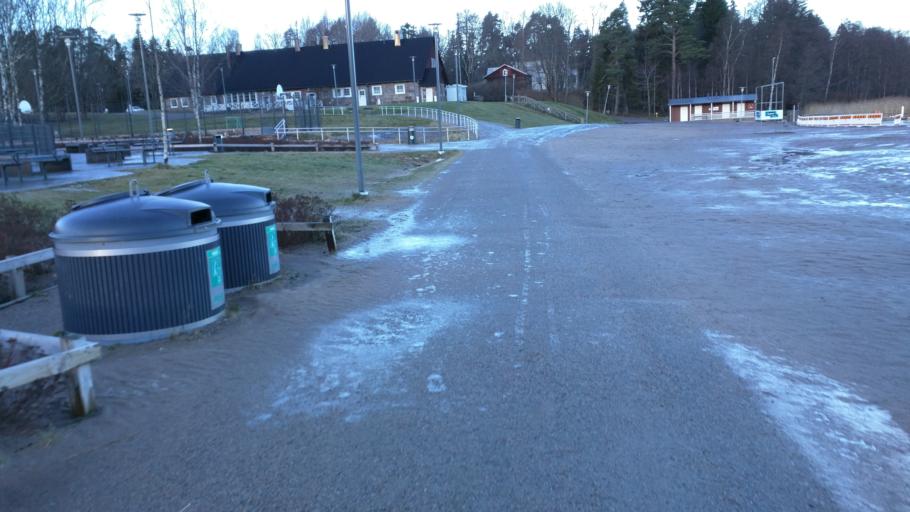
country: FI
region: Uusimaa
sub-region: Helsinki
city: Espoo
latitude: 60.2409
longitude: 24.6597
